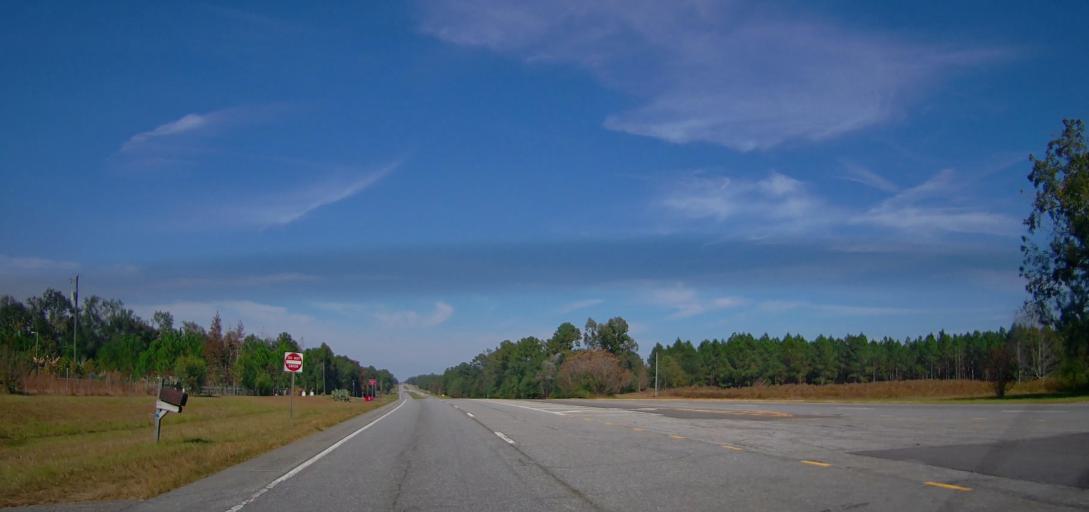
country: US
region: Georgia
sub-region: Dougherty County
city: Albany
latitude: 31.6614
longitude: -83.9978
